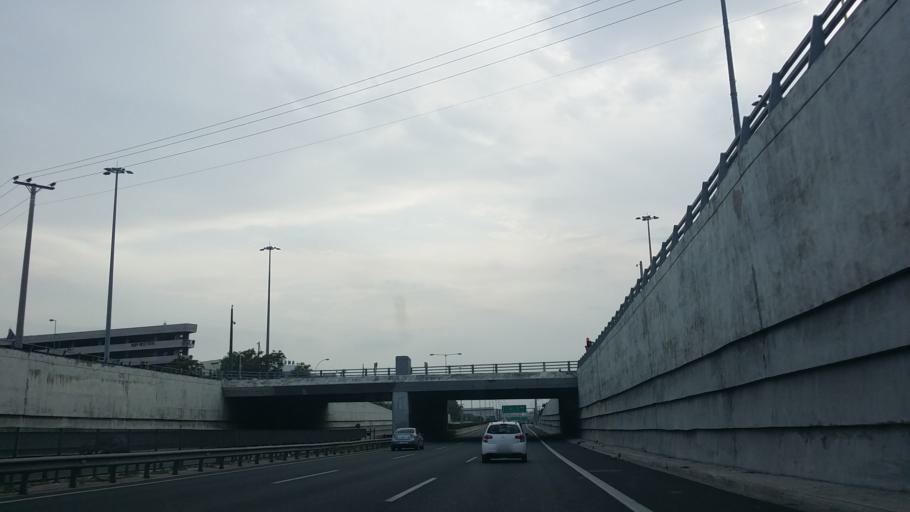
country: GR
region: Attica
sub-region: Nomarchia Athinas
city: Lykovrysi
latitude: 38.0880
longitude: 23.7883
